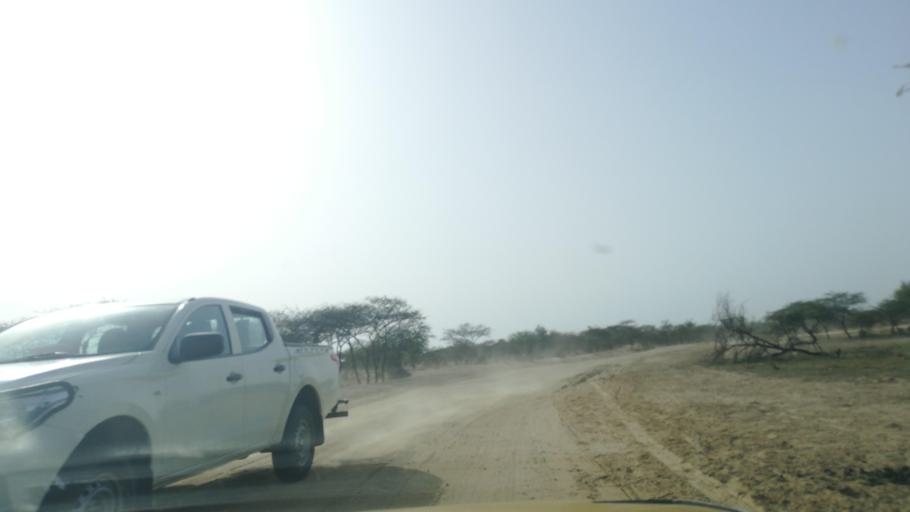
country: SN
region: Saint-Louis
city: Saint-Louis
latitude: 16.0599
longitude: -16.3331
